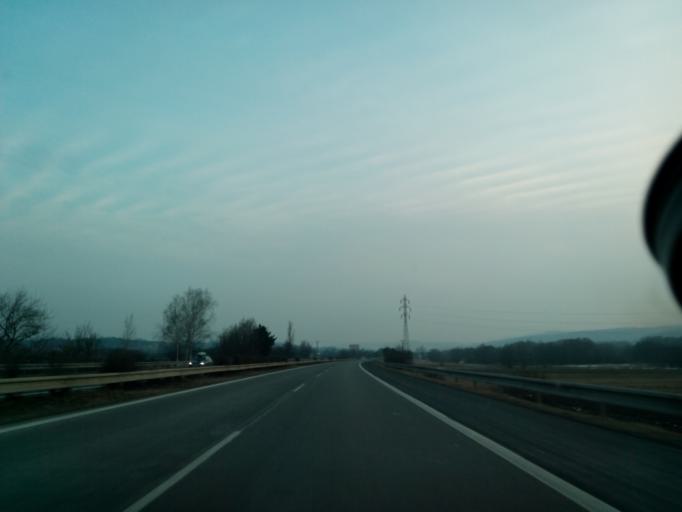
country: SK
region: Presovsky
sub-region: Okres Presov
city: Presov
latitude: 48.9346
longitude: 21.2596
